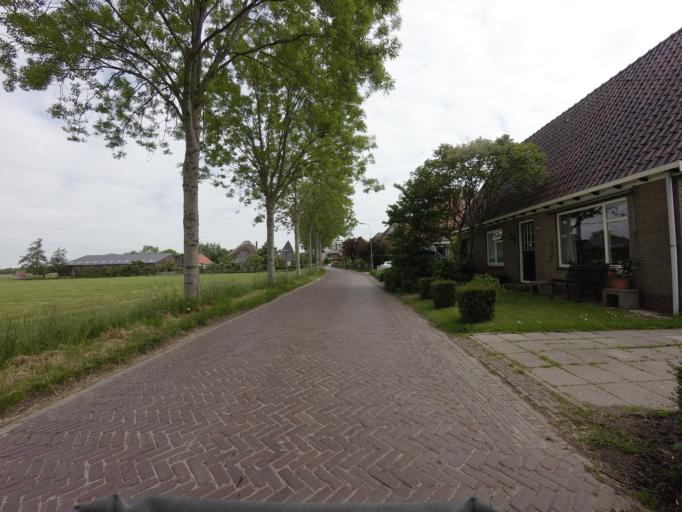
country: NL
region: North Holland
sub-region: Gemeente Medemblik
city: Opperdoes
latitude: 52.7091
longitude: 5.1058
